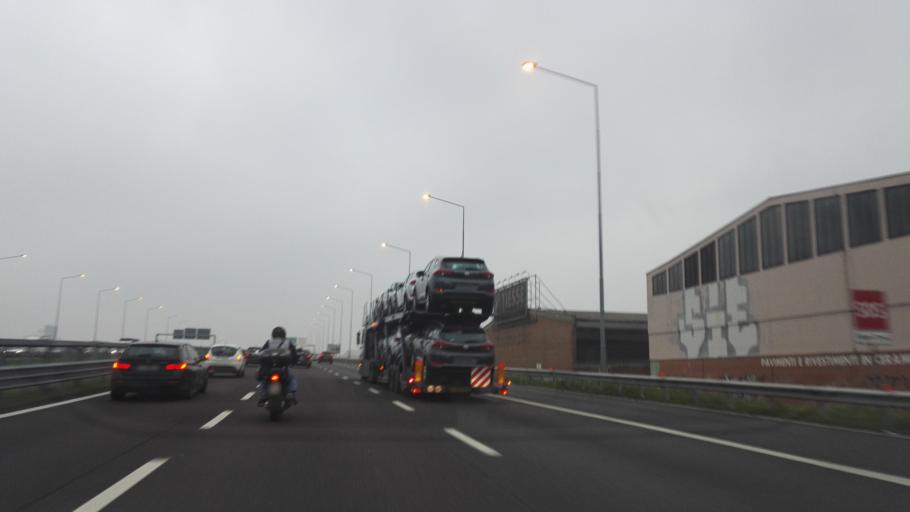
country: IT
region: Lombardy
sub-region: Citta metropolitana di Milano
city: Linate
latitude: 45.4507
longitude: 9.2580
